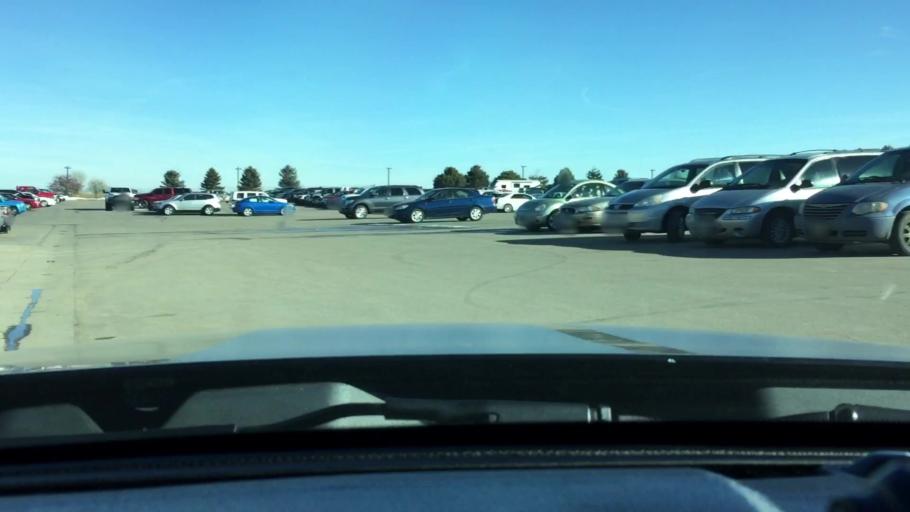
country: US
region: Colorado
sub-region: Weld County
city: Johnstown
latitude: 40.3618
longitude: -104.9769
